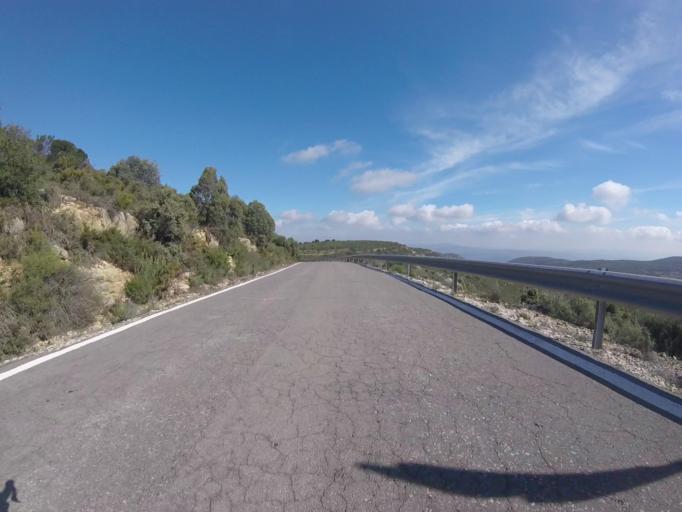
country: ES
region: Valencia
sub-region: Provincia de Castello
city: Sarratella
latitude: 40.3286
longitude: 0.0311
